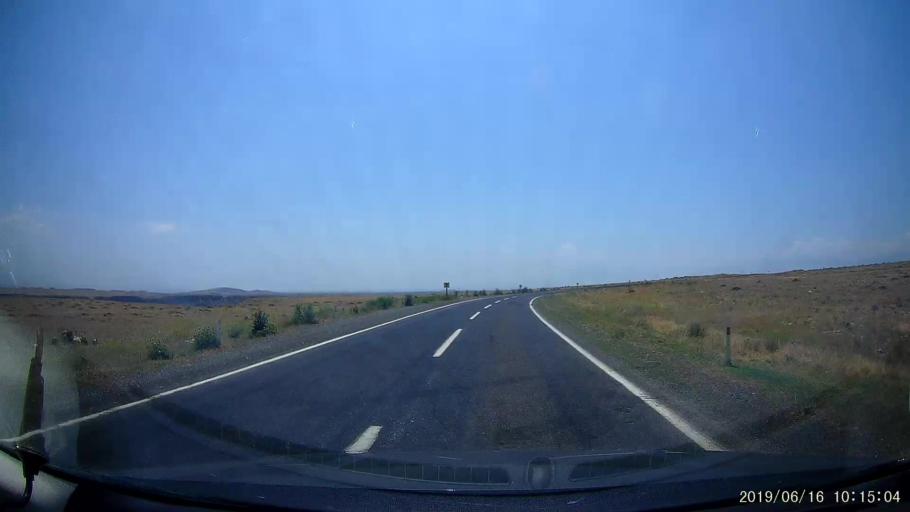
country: TR
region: Igdir
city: Tuzluca
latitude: 40.1794
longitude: 43.6755
